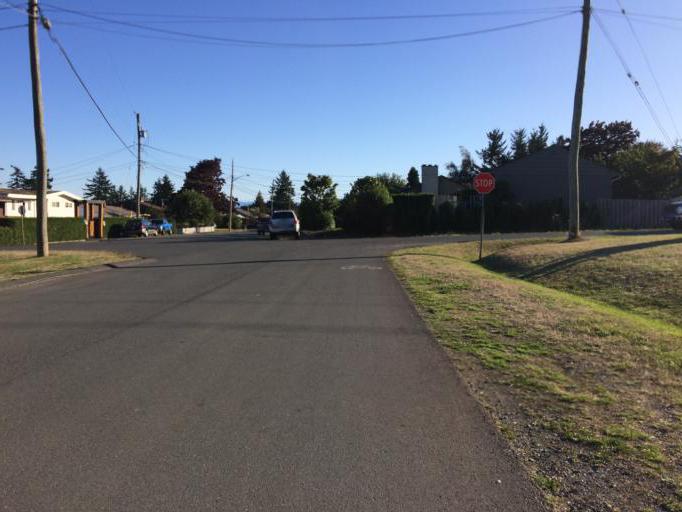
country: CA
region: British Columbia
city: Campbell River
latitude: 50.0132
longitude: -125.2368
